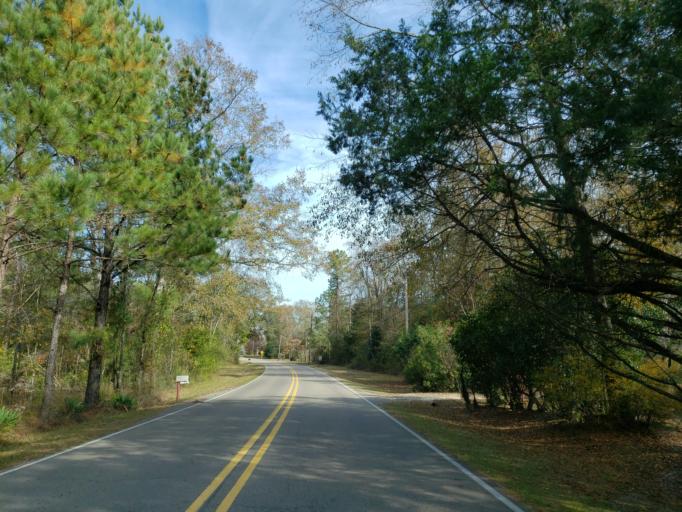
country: US
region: Mississippi
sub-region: Forrest County
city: Rawls Springs
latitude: 31.3929
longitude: -89.3708
